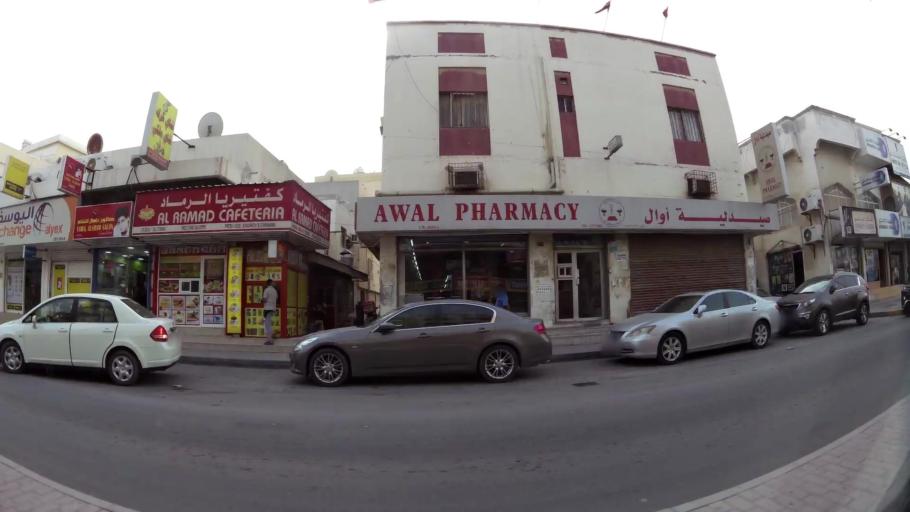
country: BH
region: Northern
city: Ar Rifa'
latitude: 26.1243
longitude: 50.5653
